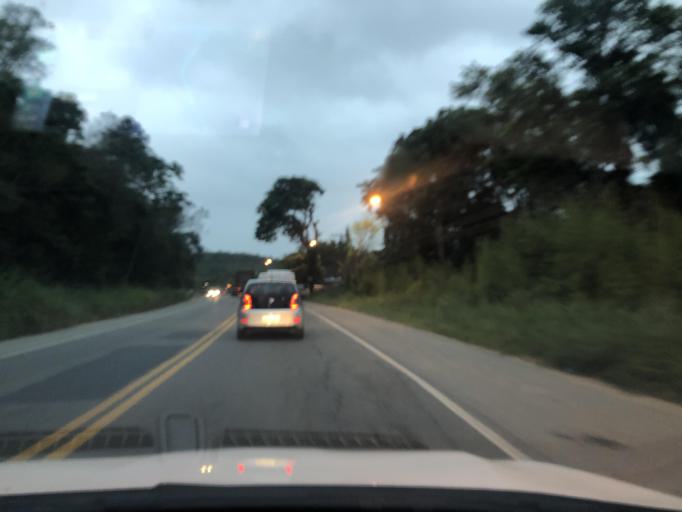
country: BR
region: Santa Catarina
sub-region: Pomerode
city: Pomerode
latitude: -26.7956
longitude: -49.0866
